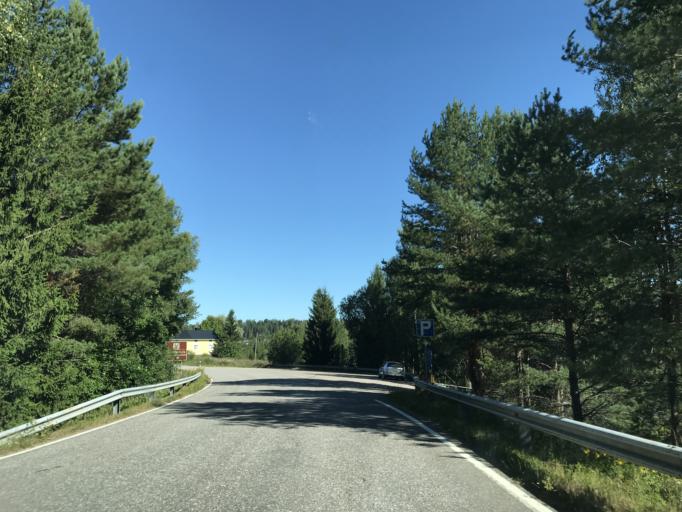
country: FI
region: Paijanne Tavastia
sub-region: Lahti
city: Orimattila
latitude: 60.7970
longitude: 25.6929
